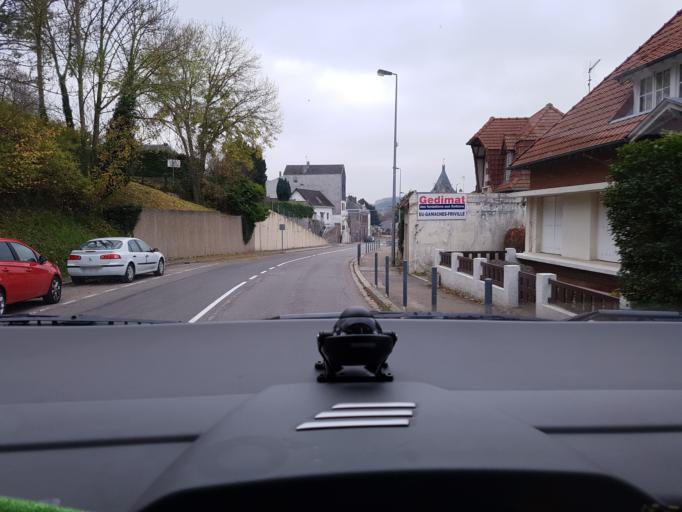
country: FR
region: Haute-Normandie
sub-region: Departement de la Seine-Maritime
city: Criel-sur-Mer
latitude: 50.0183
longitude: 1.3204
